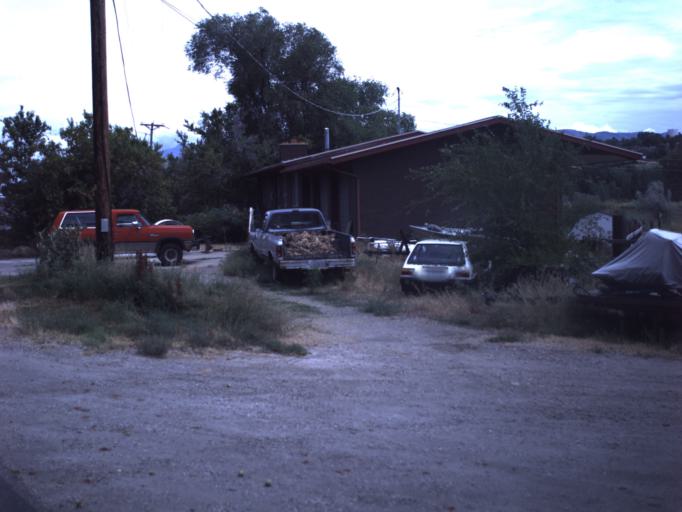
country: US
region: Utah
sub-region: Weber County
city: Riverdale
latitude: 41.1556
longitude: -111.9984
